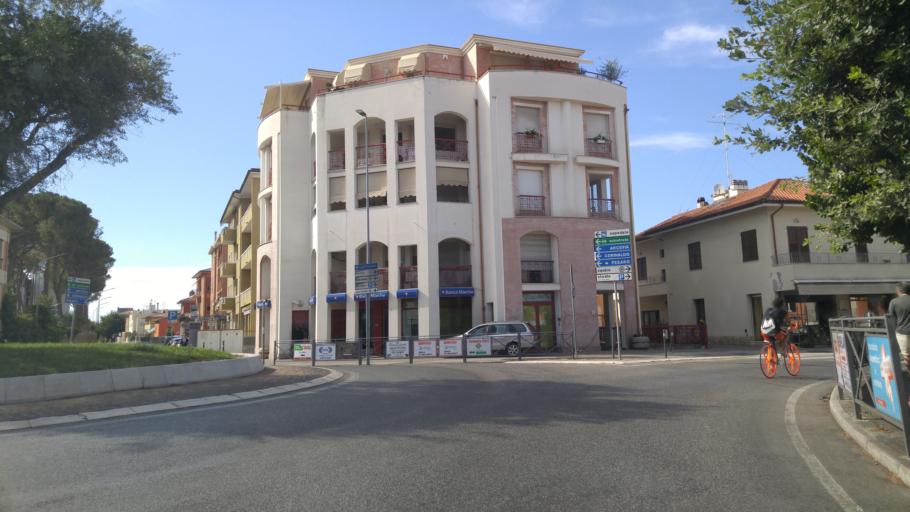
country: IT
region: The Marches
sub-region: Provincia di Ancona
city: Senigallia
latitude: 43.7141
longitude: 13.2115
